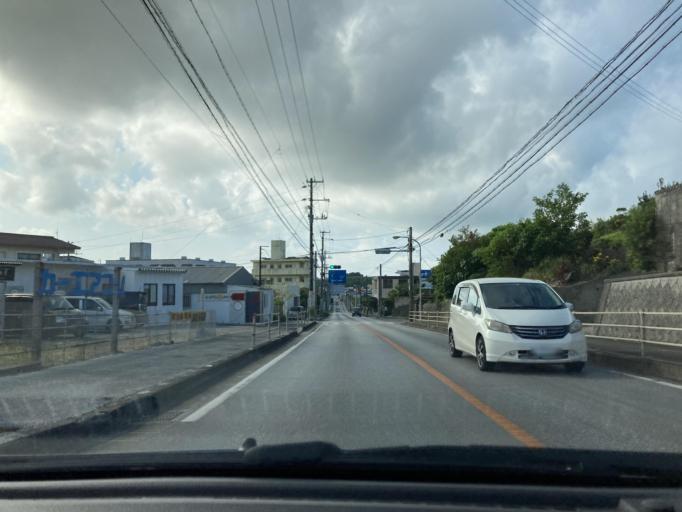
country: JP
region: Okinawa
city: Tomigusuku
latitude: 26.1646
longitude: 127.7393
